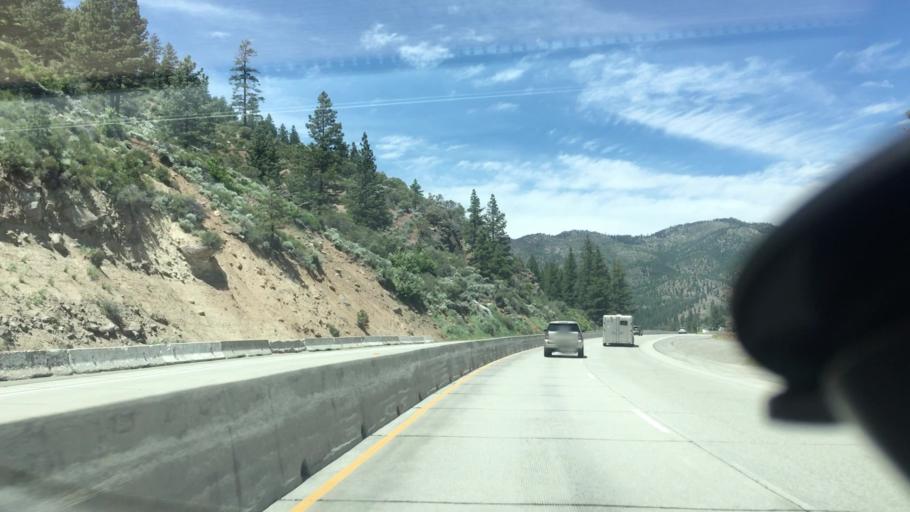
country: US
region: Nevada
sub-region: Washoe County
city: Verdi
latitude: 39.4117
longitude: -120.0280
